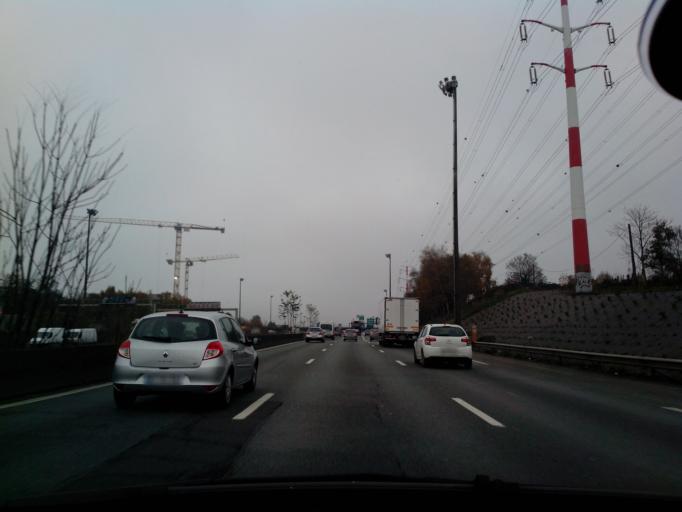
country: FR
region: Ile-de-France
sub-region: Departement du Val-de-Marne
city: Fresnes
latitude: 48.7490
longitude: 2.3281
